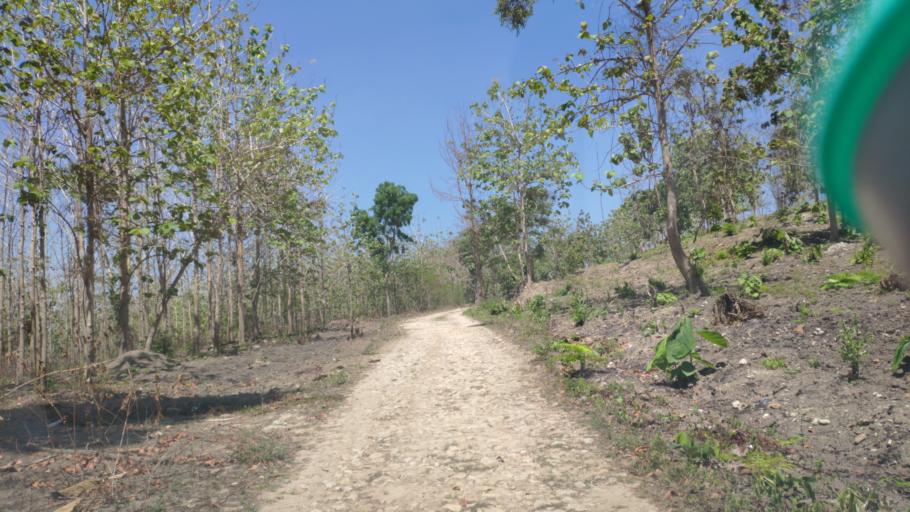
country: ID
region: Central Java
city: Suruhan
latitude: -7.0062
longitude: 111.5310
